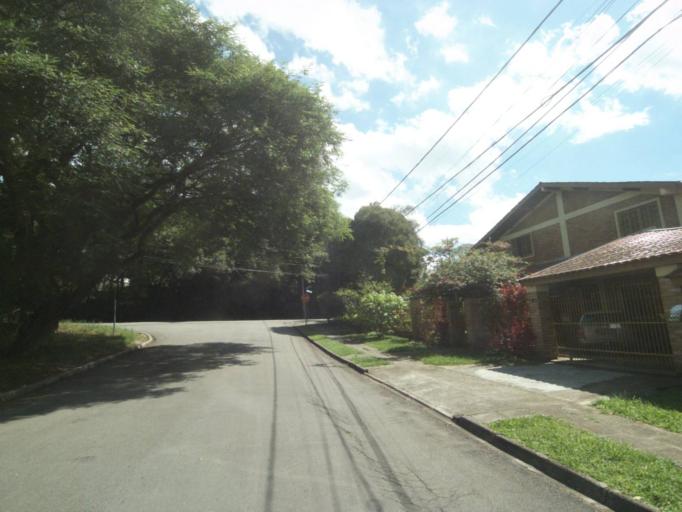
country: BR
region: Parana
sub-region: Curitiba
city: Curitiba
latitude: -25.4359
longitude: -49.3389
